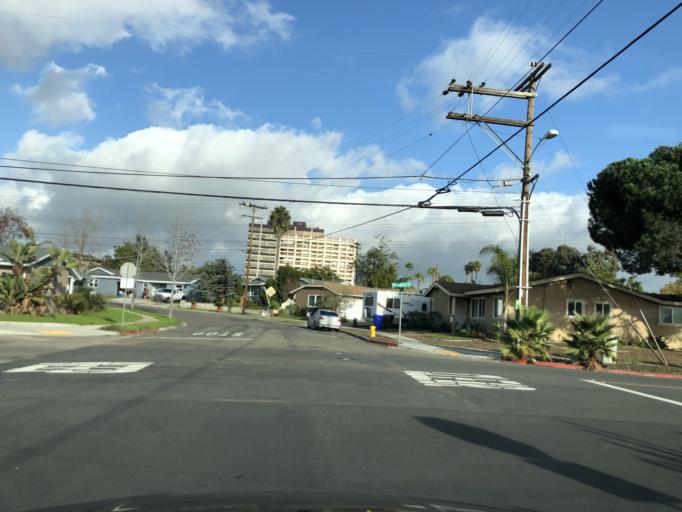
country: US
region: California
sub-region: San Diego County
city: La Jolla
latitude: 32.8184
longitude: -117.1858
